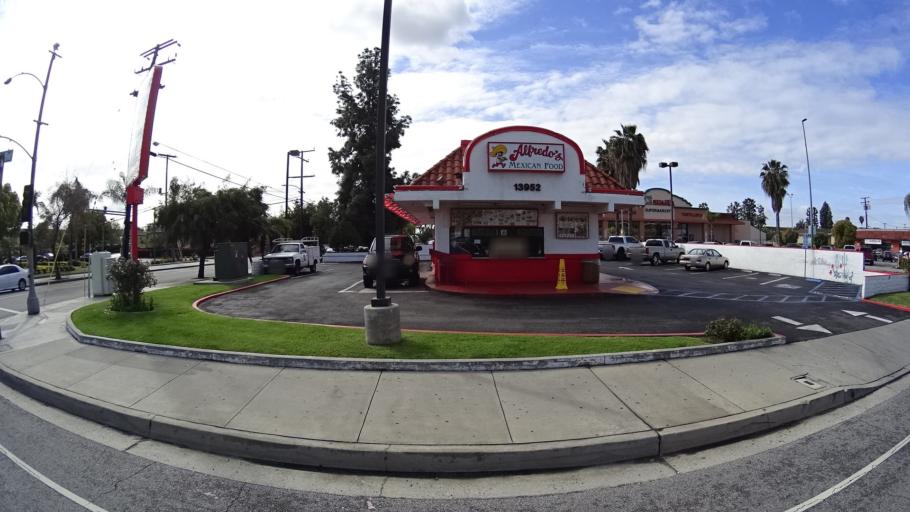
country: US
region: California
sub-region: Los Angeles County
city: Baldwin Park
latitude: 34.0843
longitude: -117.9687
